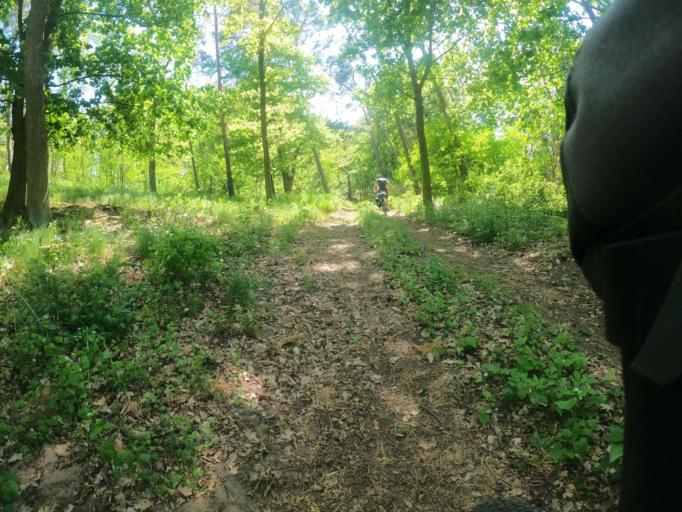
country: PL
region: West Pomeranian Voivodeship
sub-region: Powiat mysliborski
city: Barlinek
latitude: 53.0425
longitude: 15.2250
